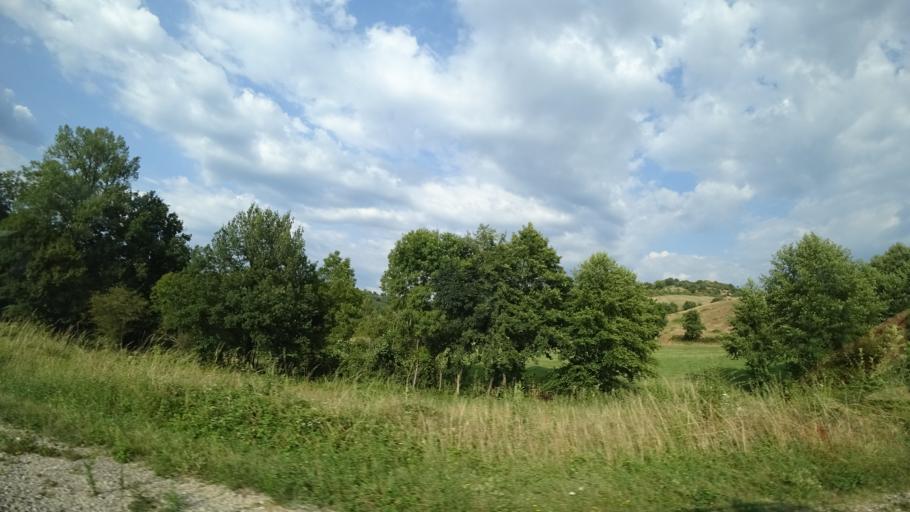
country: FR
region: Midi-Pyrenees
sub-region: Departement de l'Aveyron
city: Saint-Christophe-Vallon
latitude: 44.4923
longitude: 2.3882
